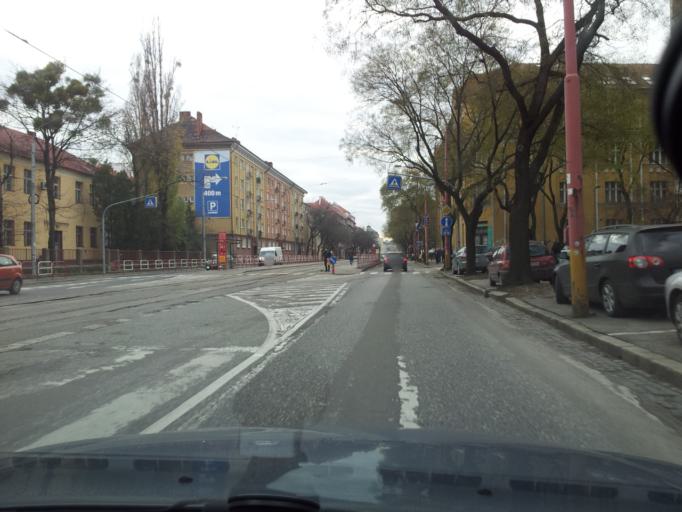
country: SK
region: Bratislavsky
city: Bratislava
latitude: 48.1624
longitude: 17.1321
